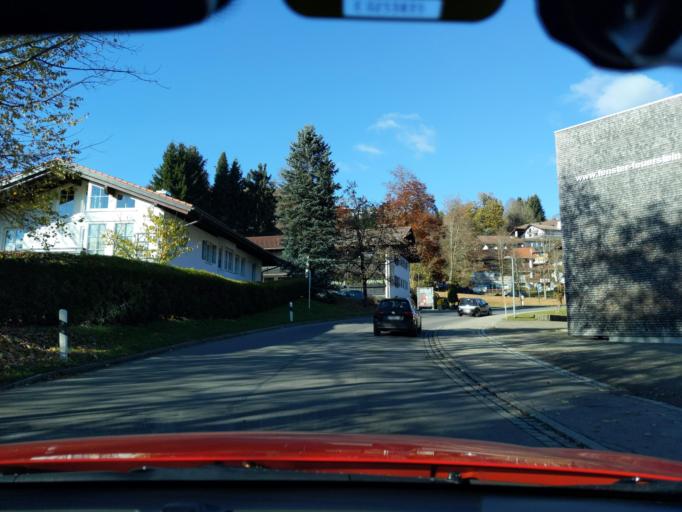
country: DE
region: Bavaria
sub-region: Swabia
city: Oberstaufen
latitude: 47.5478
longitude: 10.0216
